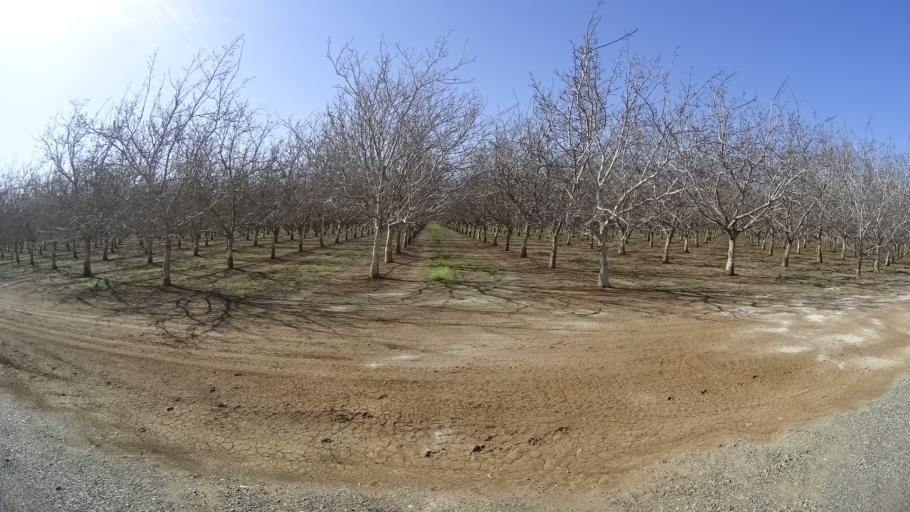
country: US
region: California
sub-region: Glenn County
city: Willows
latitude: 39.4522
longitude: -122.2438
